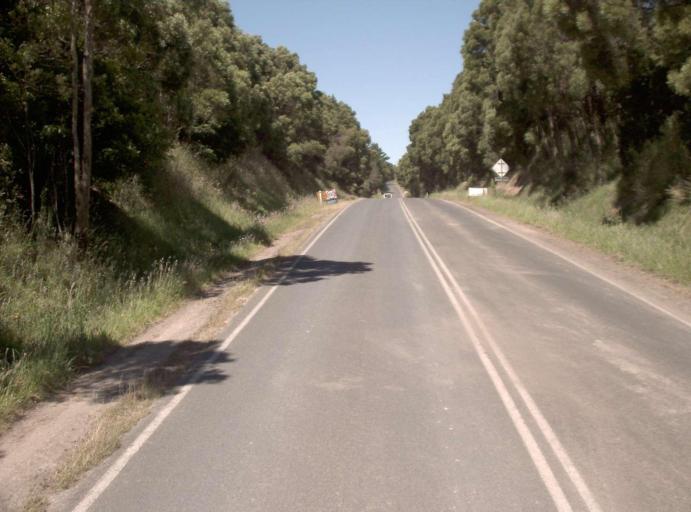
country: AU
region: Victoria
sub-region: Bass Coast
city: North Wonthaggi
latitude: -38.6949
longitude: 146.1064
